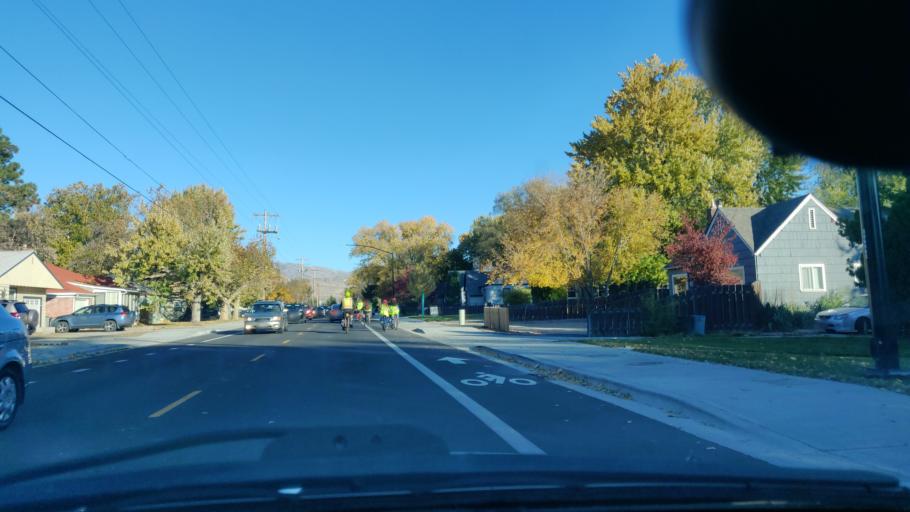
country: US
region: Idaho
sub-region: Ada County
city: Boise
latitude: 43.5935
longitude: -116.2116
